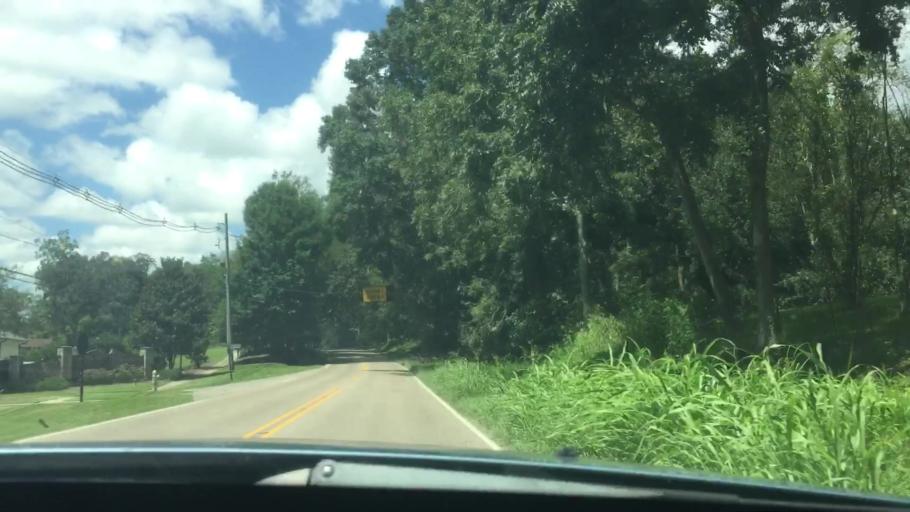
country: US
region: Louisiana
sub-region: East Baton Rouge Parish
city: Oak Hills Place
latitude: 30.3639
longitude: -91.1150
